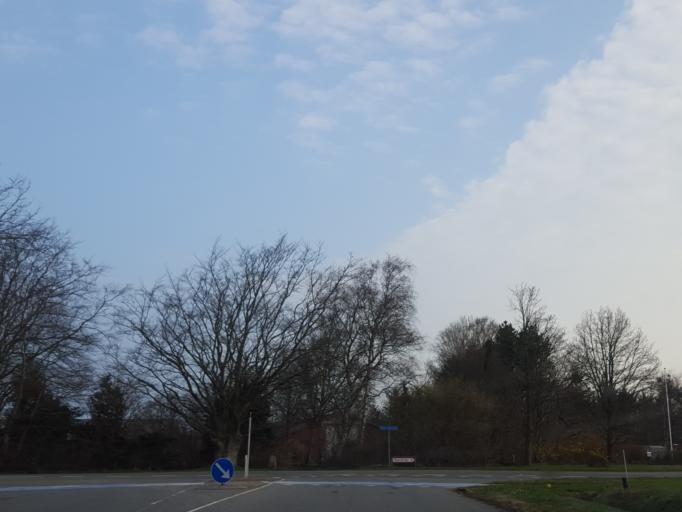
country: DK
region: South Denmark
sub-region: Esbjerg Kommune
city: Bramming
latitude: 55.4849
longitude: 8.7027
